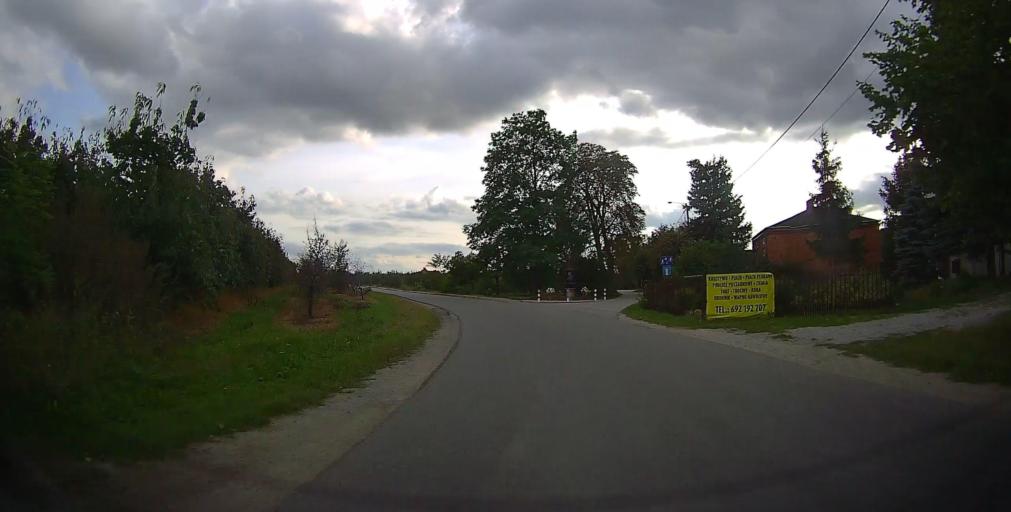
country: PL
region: Masovian Voivodeship
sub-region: Powiat bialobrzeski
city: Promna
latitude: 51.7233
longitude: 20.9590
